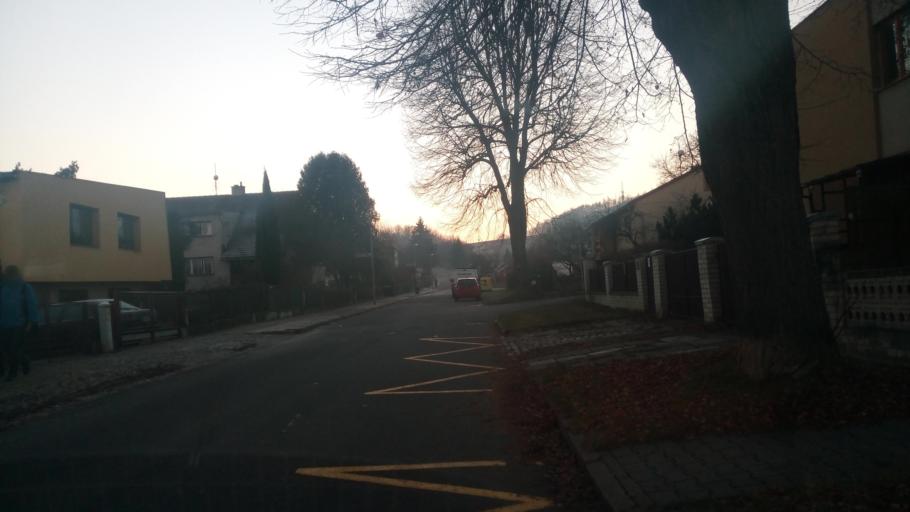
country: CZ
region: Olomoucky
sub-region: Okres Sumperk
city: Sumperk
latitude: 49.9634
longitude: 16.9603
